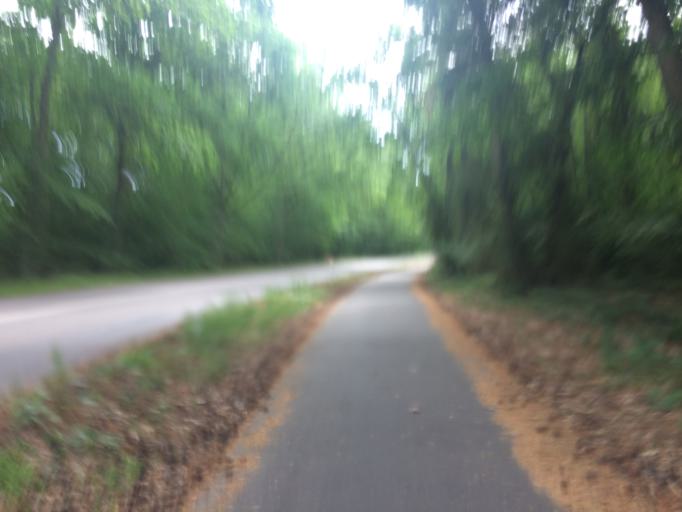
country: DK
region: Capital Region
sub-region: Bornholm Kommune
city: Ronne
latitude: 55.1653
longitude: 14.7155
